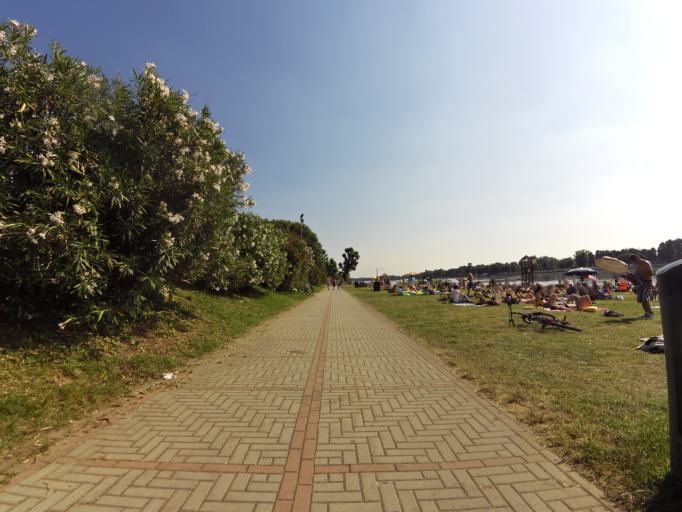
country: IT
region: Lombardy
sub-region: Citta metropolitana di Milano
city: Novegro-Tregarezzo-San Felice
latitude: 45.4746
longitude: 9.2929
